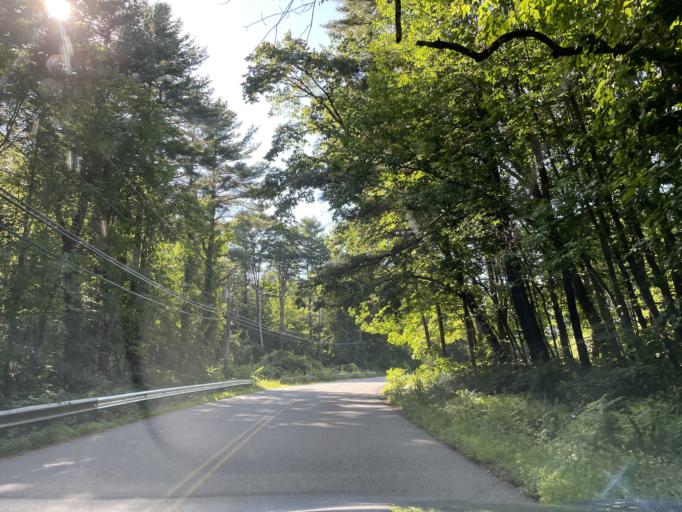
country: US
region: Massachusetts
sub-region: Worcester County
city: Charlton
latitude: 42.1528
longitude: -71.9949
